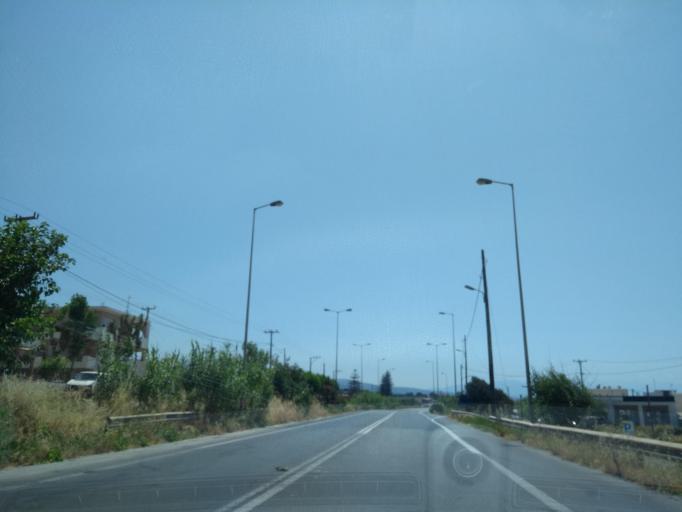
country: GR
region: Crete
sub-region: Nomos Rethymnis
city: Rethymno
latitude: 35.3808
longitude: 24.5811
